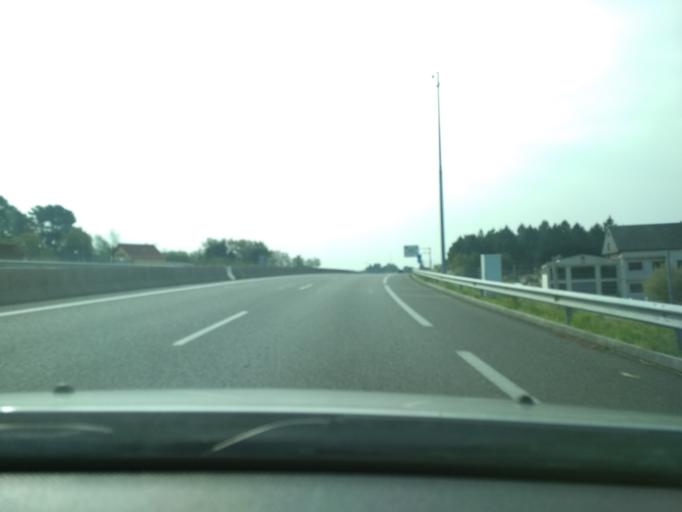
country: ES
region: Galicia
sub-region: Provincia da Coruna
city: Rianxo
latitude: 42.6726
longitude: -8.8302
